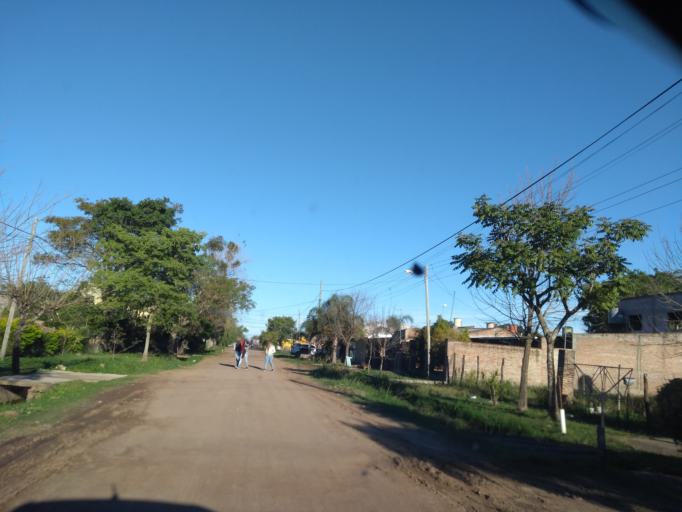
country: AR
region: Chaco
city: Barranqueras
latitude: -27.4885
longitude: -58.9420
